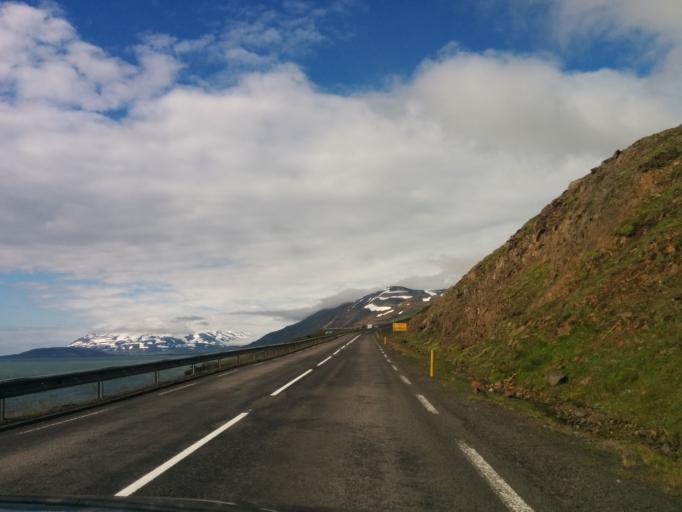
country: IS
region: Northeast
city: Akureyri
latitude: 65.7962
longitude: -18.0586
